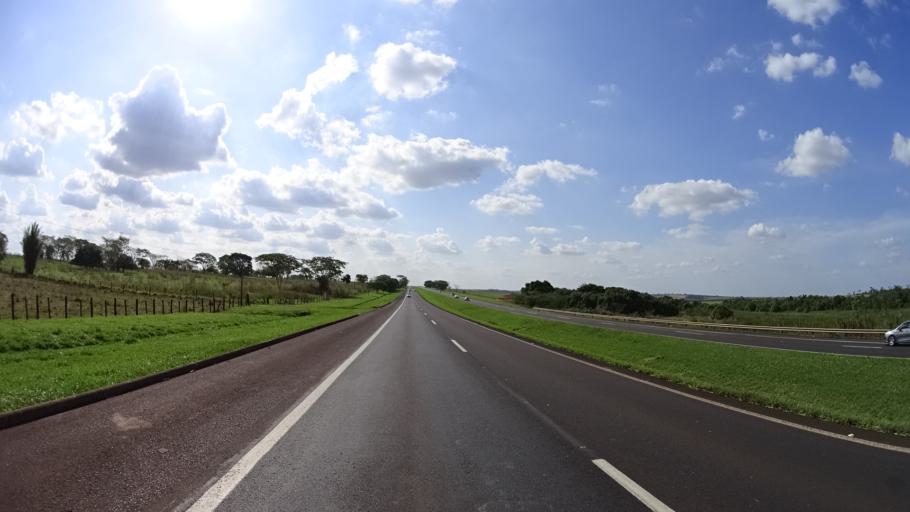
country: BR
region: Sao Paulo
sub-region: Guapiacu
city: Guapiacu
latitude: -20.9778
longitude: -49.2225
